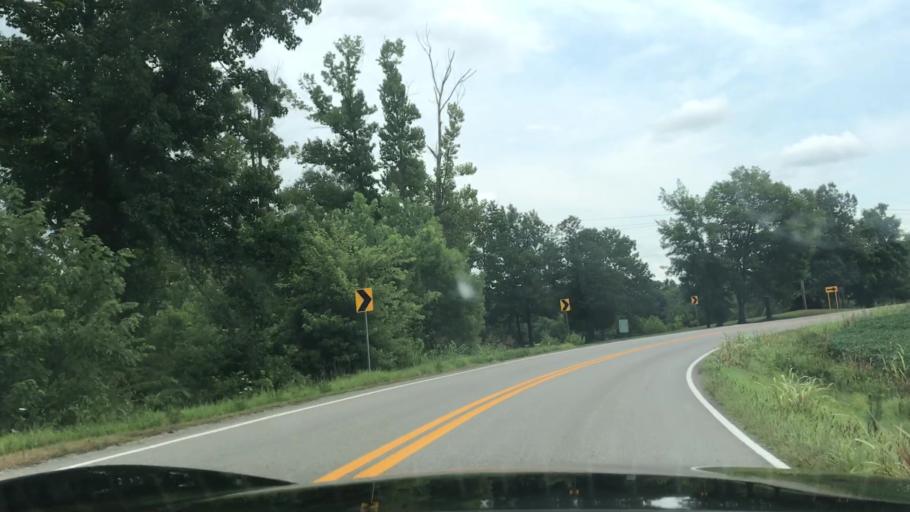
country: US
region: Kentucky
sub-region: Ohio County
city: Beaver Dam
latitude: 37.2141
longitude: -86.9031
